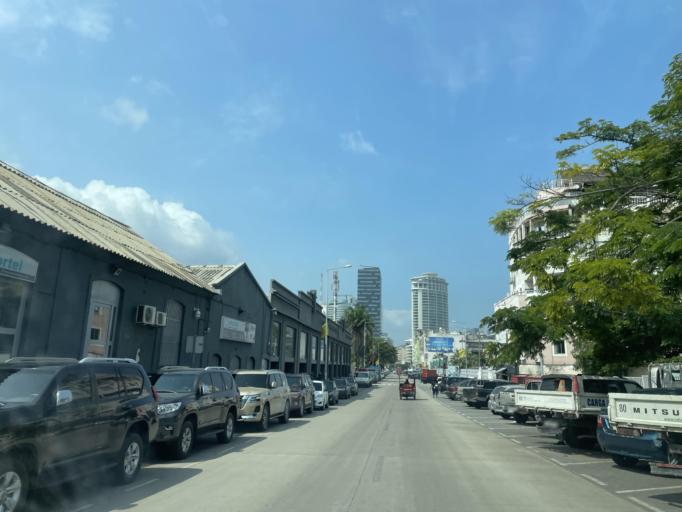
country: AO
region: Luanda
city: Luanda
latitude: -8.8055
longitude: 13.2436
